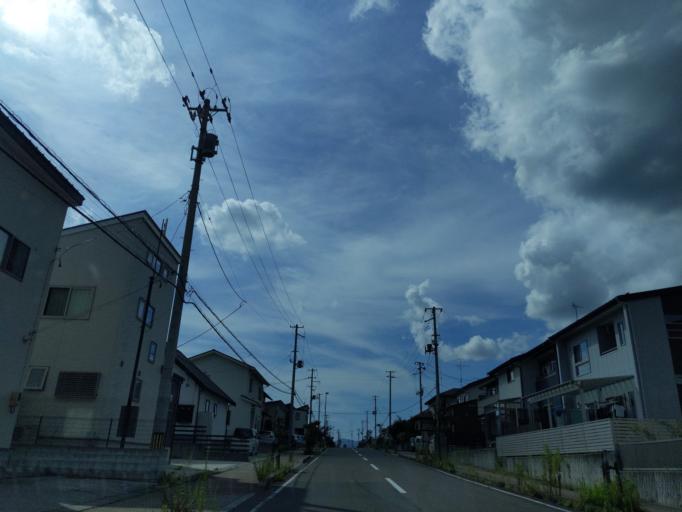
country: JP
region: Fukushima
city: Koriyama
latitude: 37.3517
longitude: 140.3381
